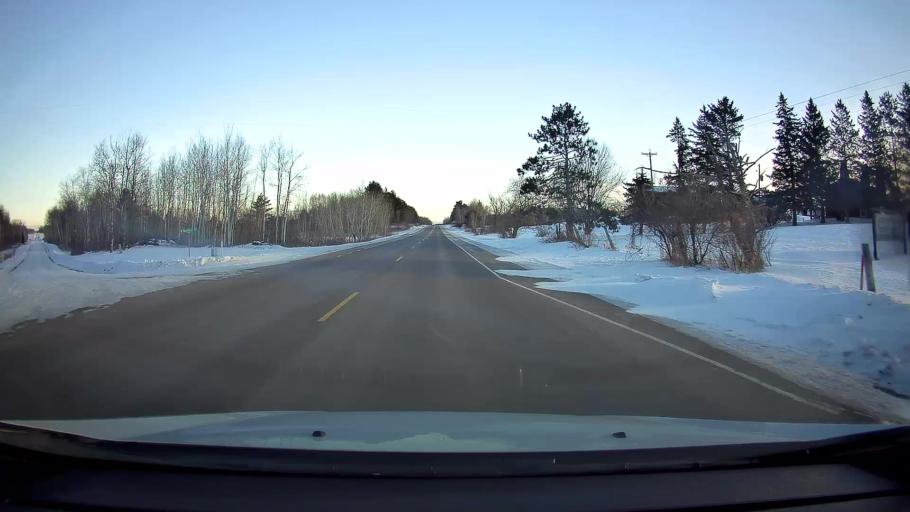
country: US
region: Wisconsin
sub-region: Washburn County
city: Shell Lake
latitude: 45.6908
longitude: -91.9705
